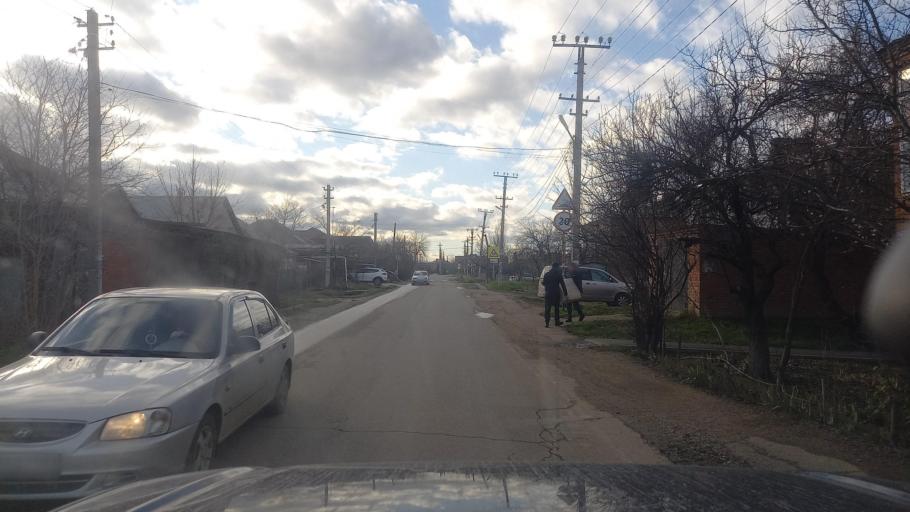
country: RU
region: Adygeya
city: Yablonovskiy
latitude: 44.9875
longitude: 38.9324
